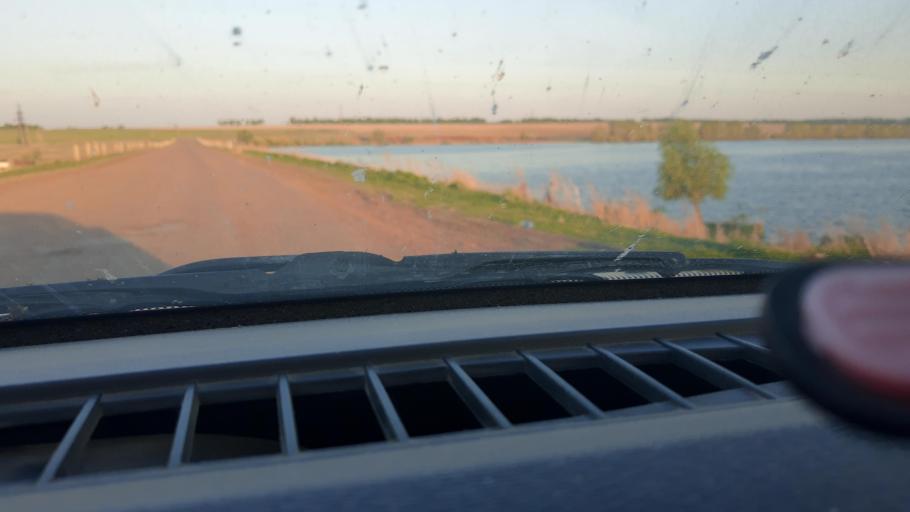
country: RU
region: Bashkortostan
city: Asanovo
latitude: 54.8525
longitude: 55.5871
